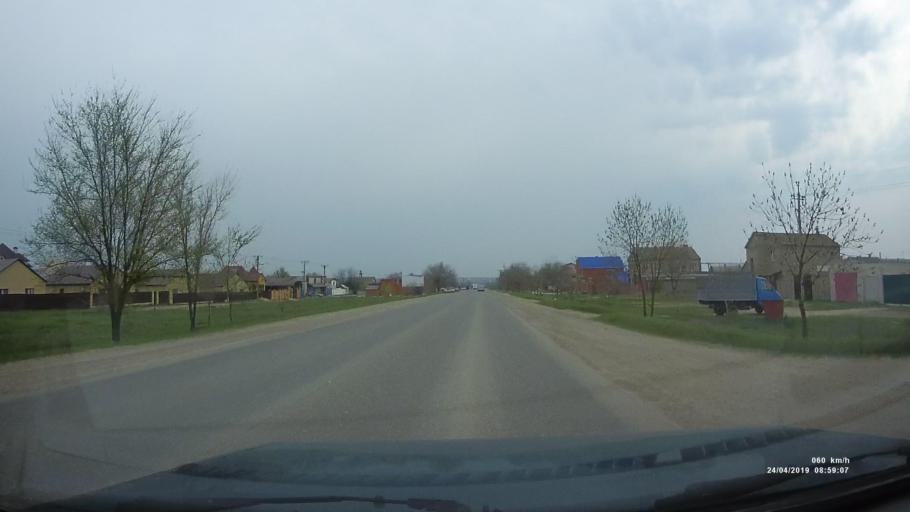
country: RU
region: Kalmykiya
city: Arshan'
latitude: 46.3121
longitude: 44.2053
